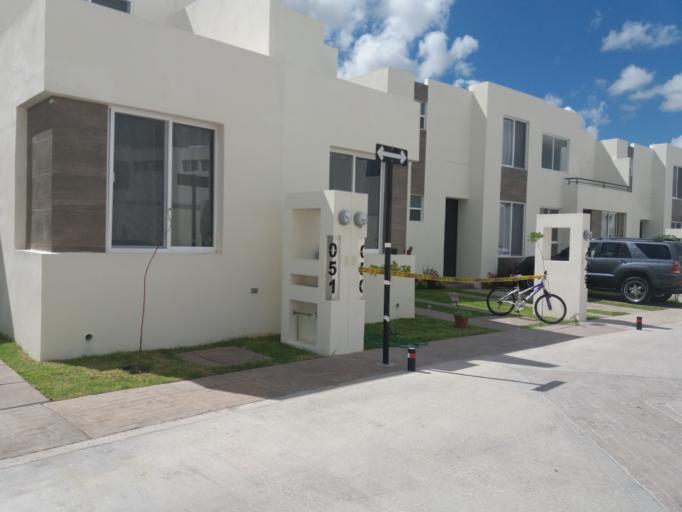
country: MX
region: Aguascalientes
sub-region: Aguascalientes
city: San Sebastian [Fraccionamiento]
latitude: 21.8189
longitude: -102.2727
